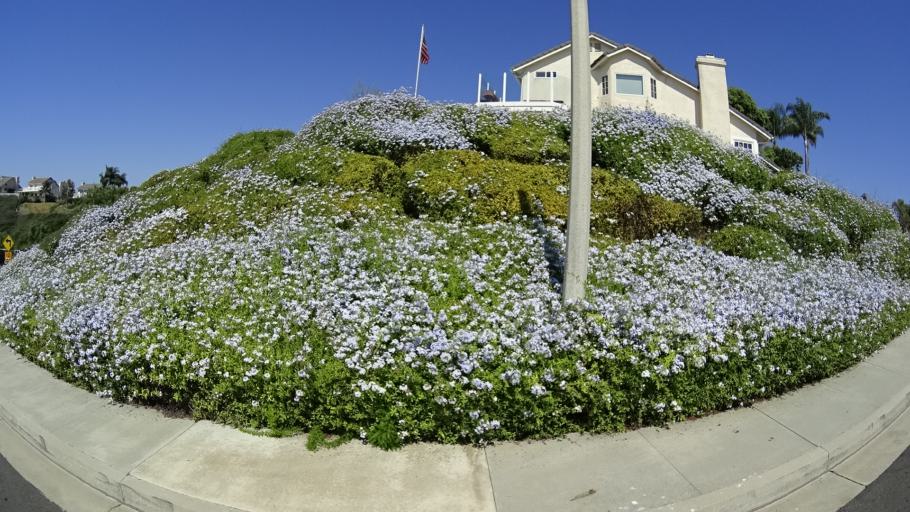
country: US
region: California
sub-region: Orange County
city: San Clemente
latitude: 33.4587
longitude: -117.6269
